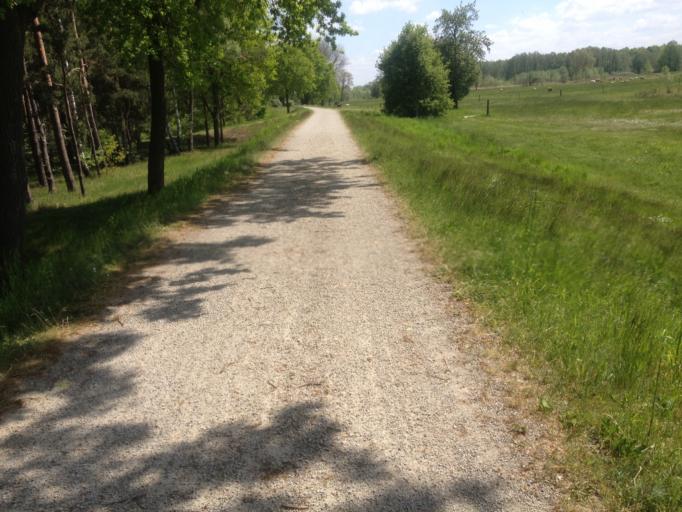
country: DE
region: Brandenburg
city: Drehnow
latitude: 51.8505
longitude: 14.3200
